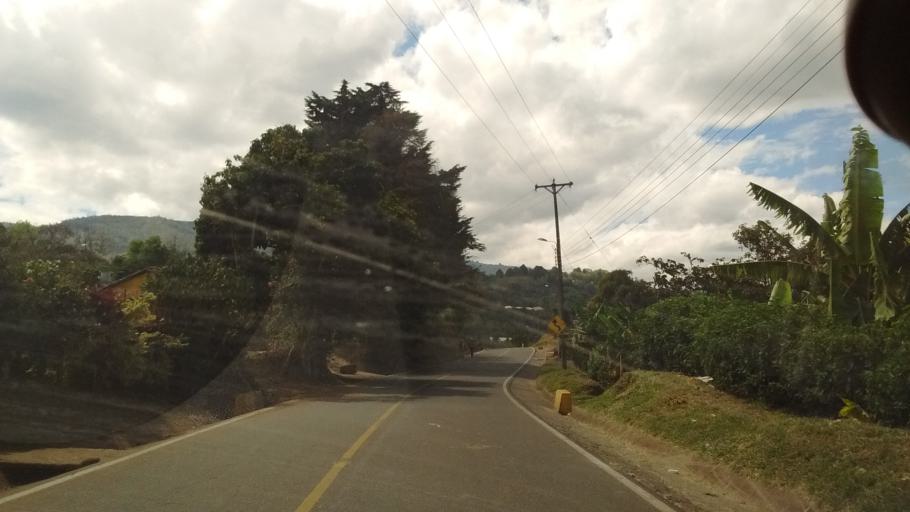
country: CO
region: Cauca
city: Cajibio
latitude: 2.6289
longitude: -76.5194
